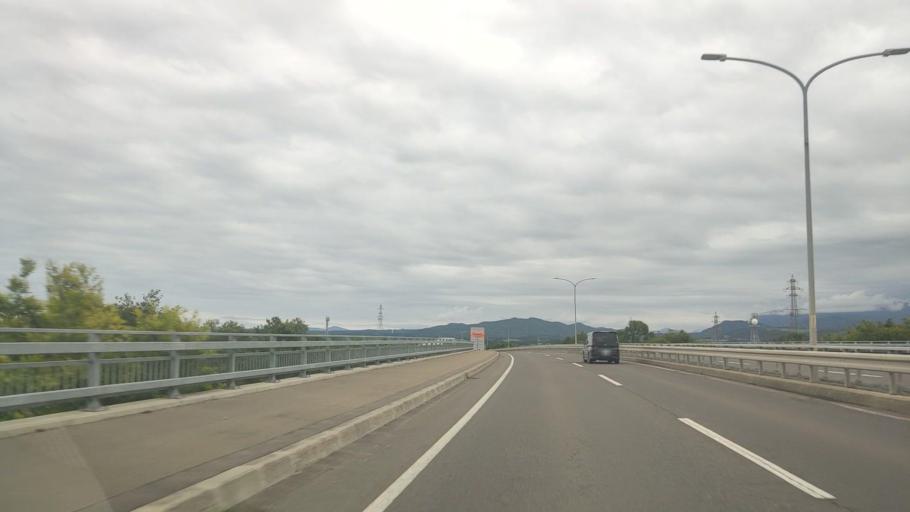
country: JP
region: Hokkaido
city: Nanae
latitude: 42.2648
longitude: 140.2730
